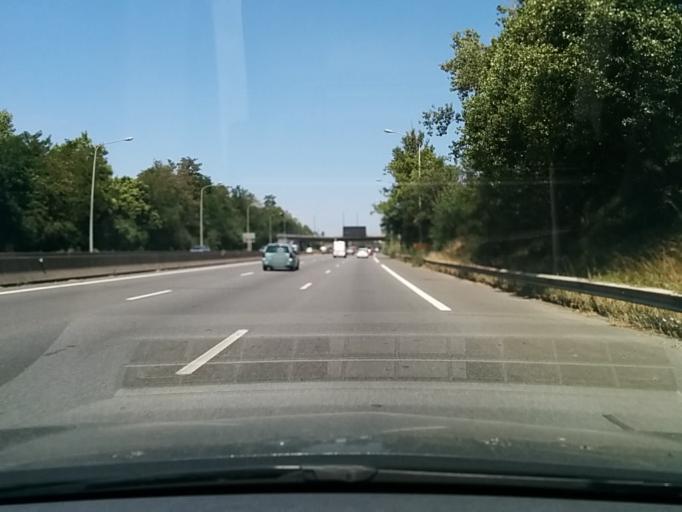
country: FR
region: Midi-Pyrenees
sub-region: Departement de la Haute-Garonne
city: Blagnac
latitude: 43.5896
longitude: 1.3999
